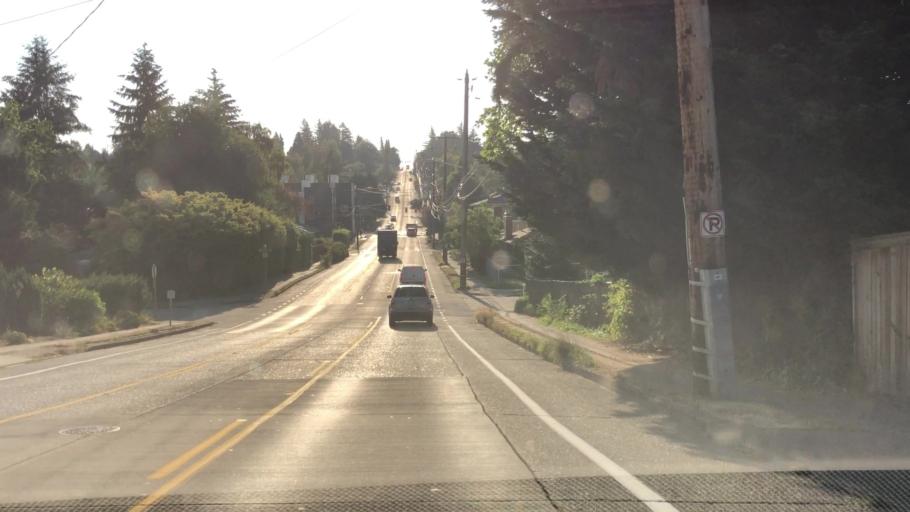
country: US
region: Washington
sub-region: King County
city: Lake Forest Park
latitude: 47.6830
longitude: -122.3036
